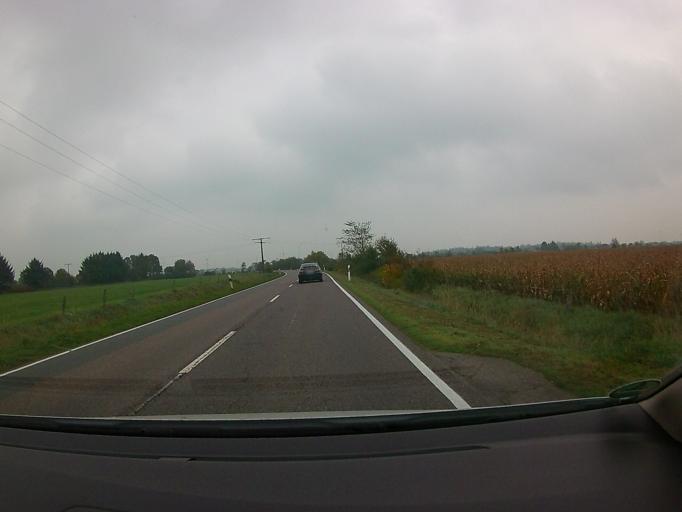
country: DE
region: Schleswig-Holstein
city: Goldebek
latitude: 54.6757
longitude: 9.1555
